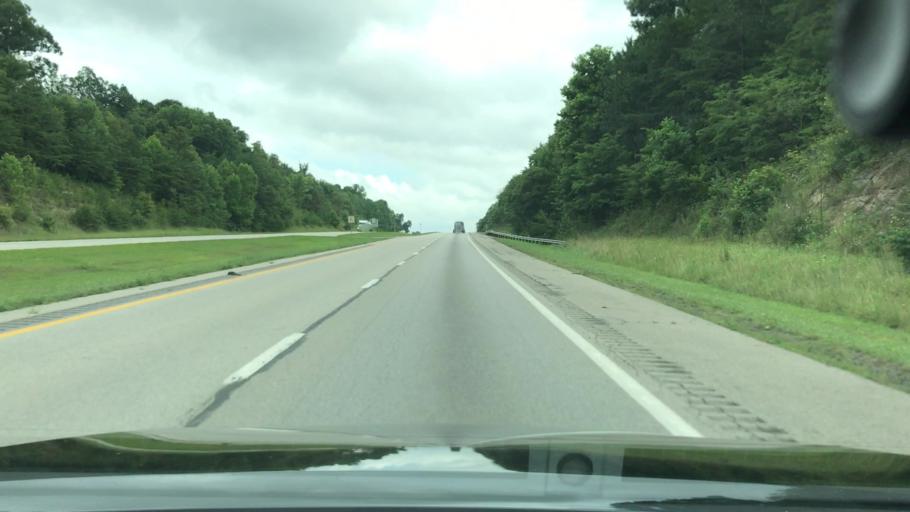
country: US
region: Ohio
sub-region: Jackson County
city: Jackson
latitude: 39.0895
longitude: -82.6486
